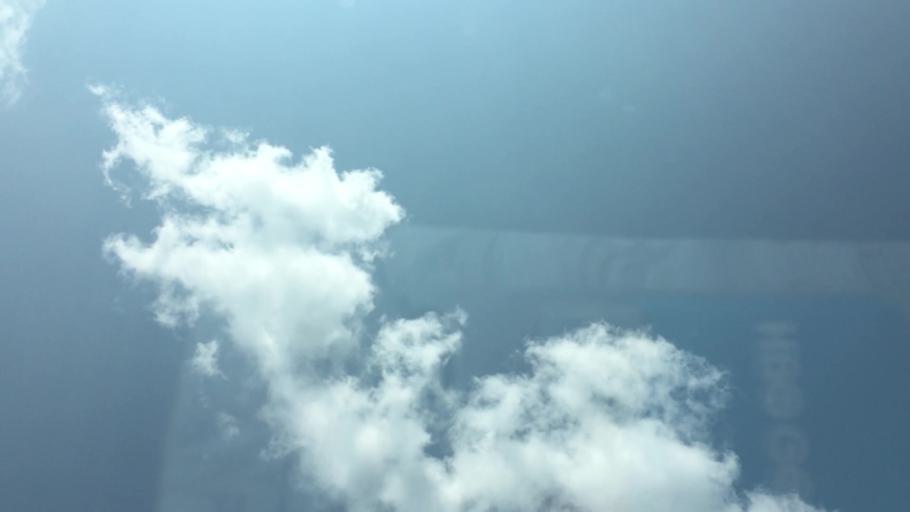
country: US
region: Alabama
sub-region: Pickens County
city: Gordo
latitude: 33.2783
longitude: -87.7749
